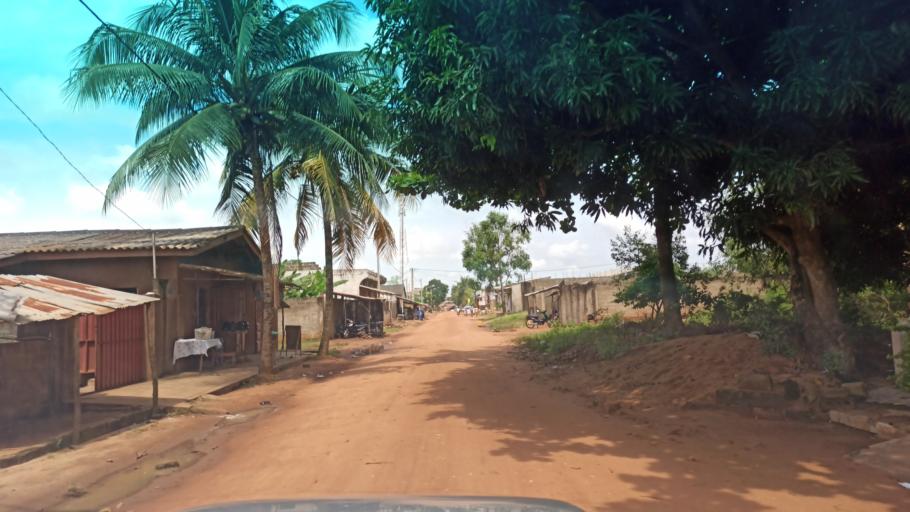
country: BJ
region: Queme
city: Porto-Novo
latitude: 6.4988
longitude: 2.5880
